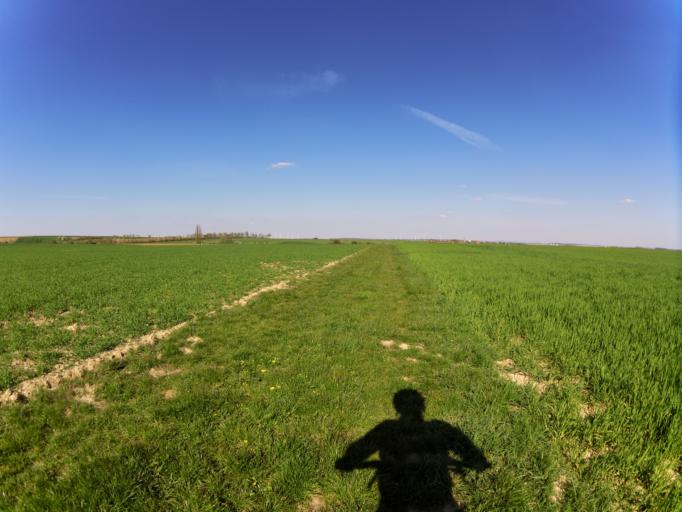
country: DE
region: Bavaria
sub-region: Regierungsbezirk Unterfranken
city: Kurnach
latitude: 49.8685
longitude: 10.0080
